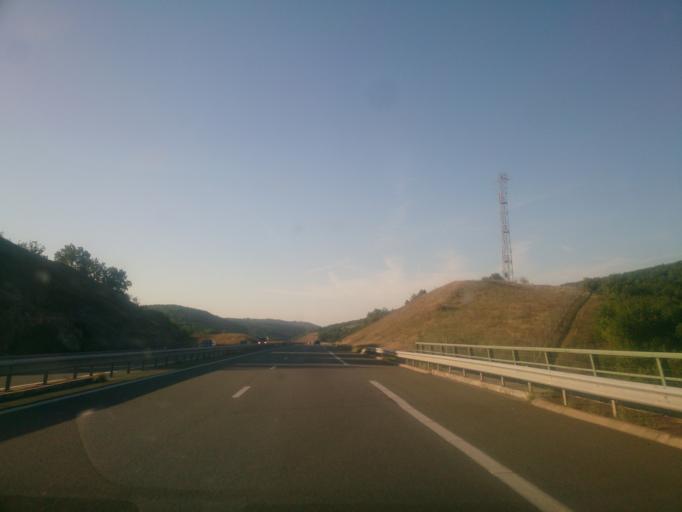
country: FR
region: Midi-Pyrenees
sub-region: Departement du Lot
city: Le Vigan
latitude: 44.8071
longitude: 1.5050
